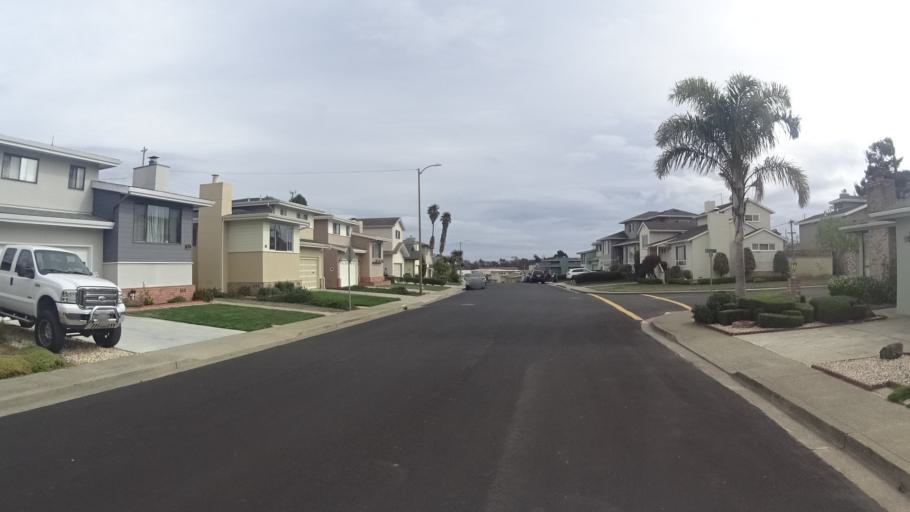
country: US
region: California
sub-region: San Mateo County
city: South San Francisco
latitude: 37.6486
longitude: -122.4344
